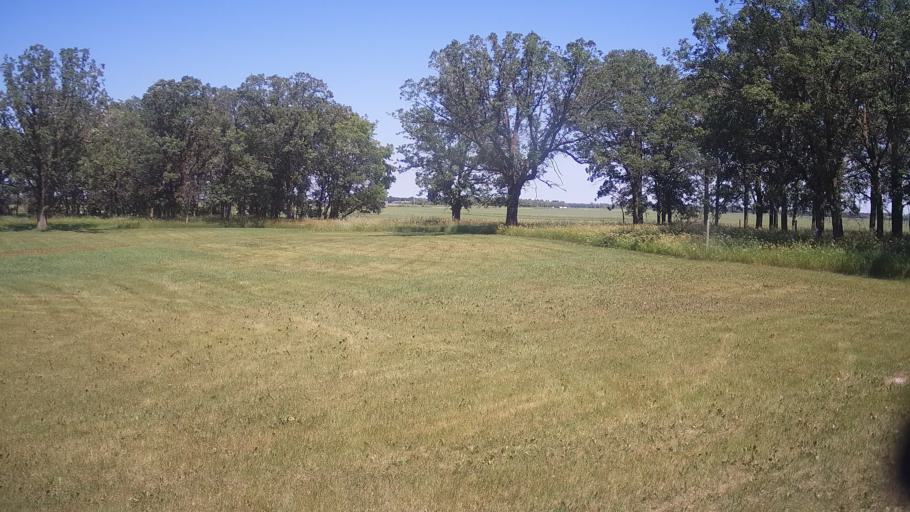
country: CA
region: Manitoba
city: Stonewall
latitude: 50.1246
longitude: -97.4748
